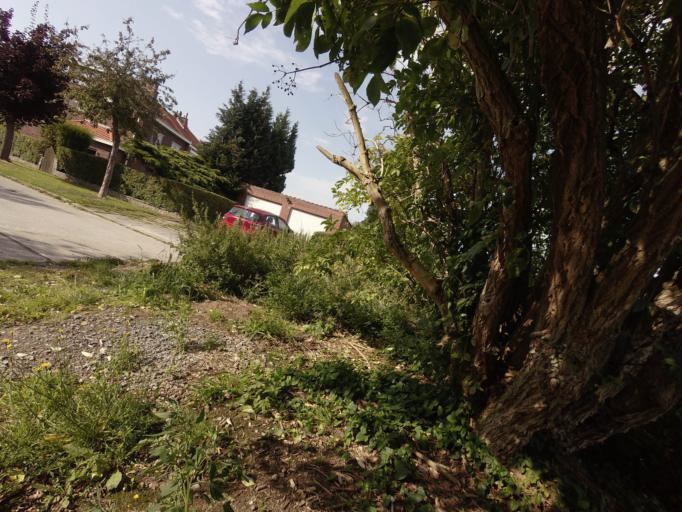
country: BE
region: Flanders
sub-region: Provincie Vlaams-Brabant
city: Grimbergen
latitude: 50.9043
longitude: 4.3672
